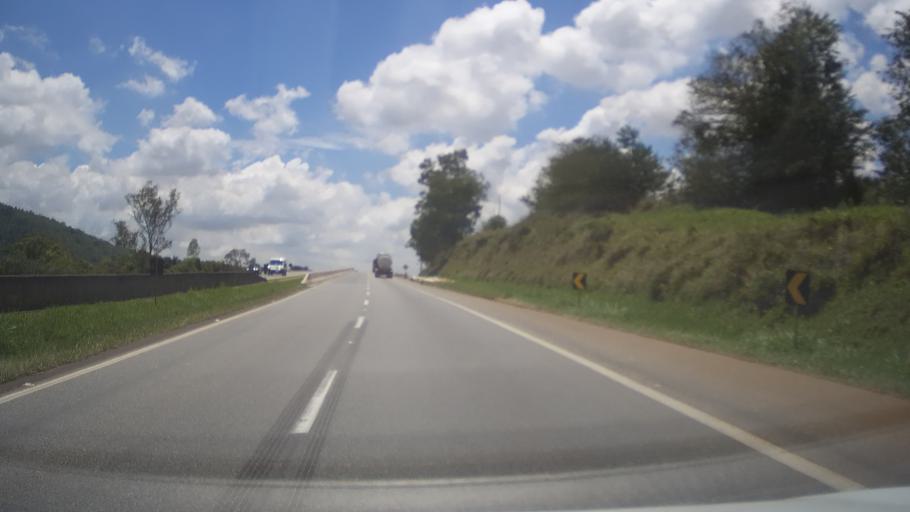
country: BR
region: Minas Gerais
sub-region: Campanha
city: Campanha
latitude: -21.8041
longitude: -45.4738
